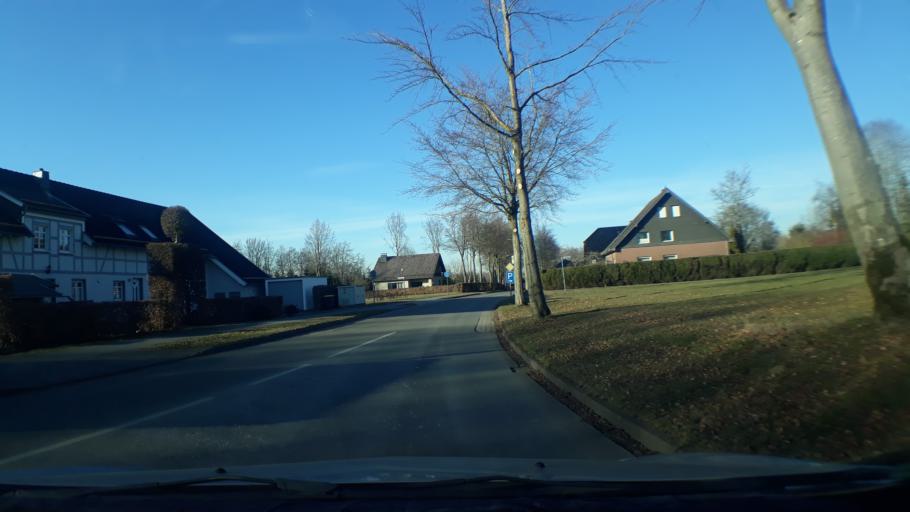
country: DE
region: North Rhine-Westphalia
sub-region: Regierungsbezirk Koln
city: Monschau
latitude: 50.5443
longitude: 6.2841
